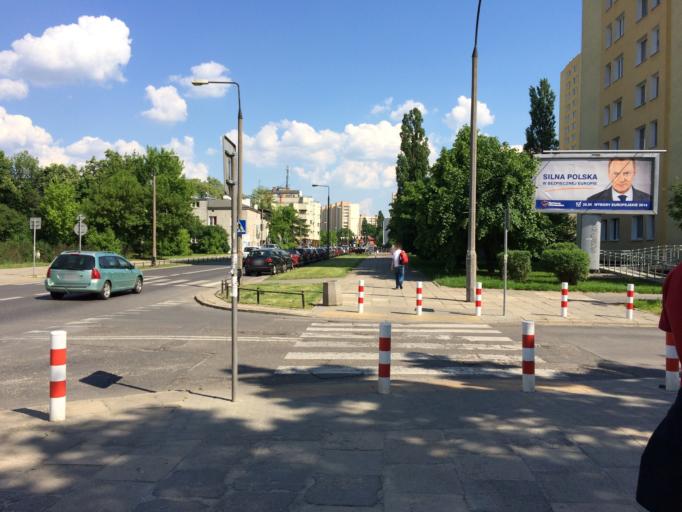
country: PL
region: Masovian Voivodeship
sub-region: Warszawa
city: Praga Poludnie
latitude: 52.2378
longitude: 21.1011
